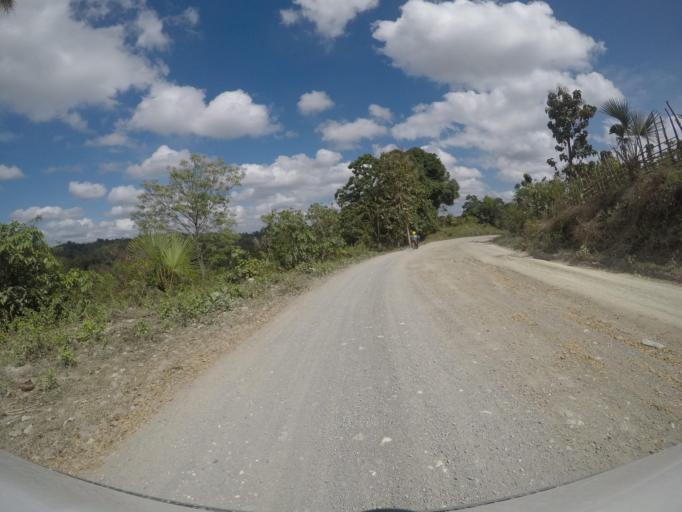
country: TL
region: Viqueque
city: Viqueque
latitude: -8.8714
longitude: 126.3440
